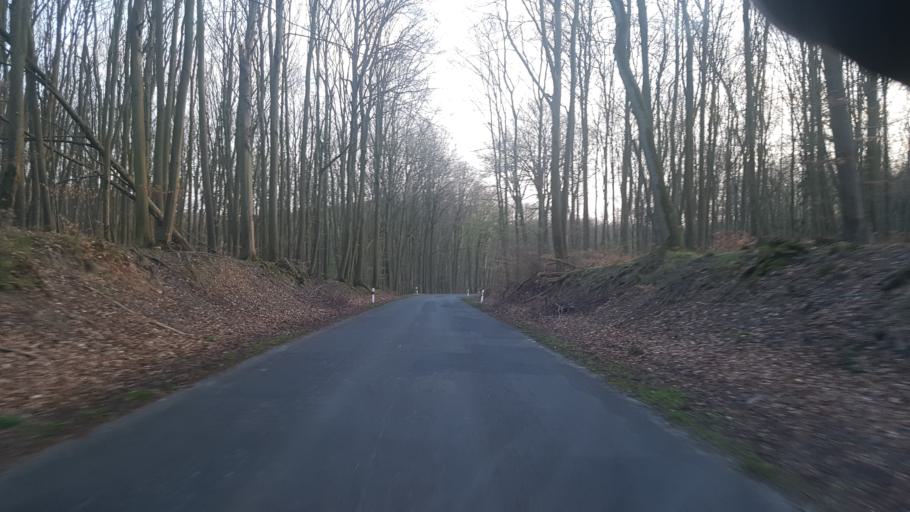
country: DE
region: Brandenburg
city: Gramzow
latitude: 53.1843
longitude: 13.9125
